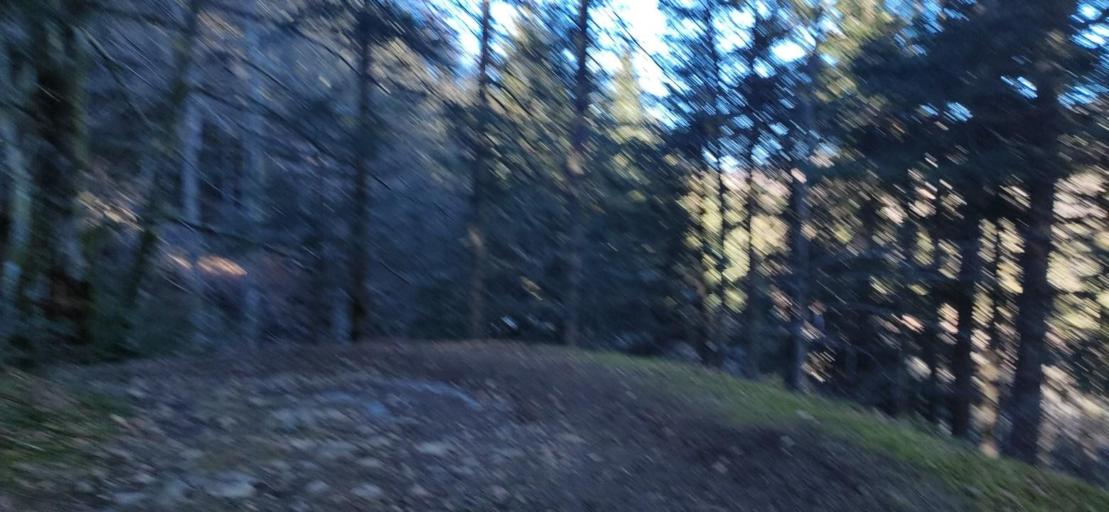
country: FR
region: Auvergne
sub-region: Departement du Puy-de-Dome
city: Mont-Dore
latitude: 45.5690
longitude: 2.8081
